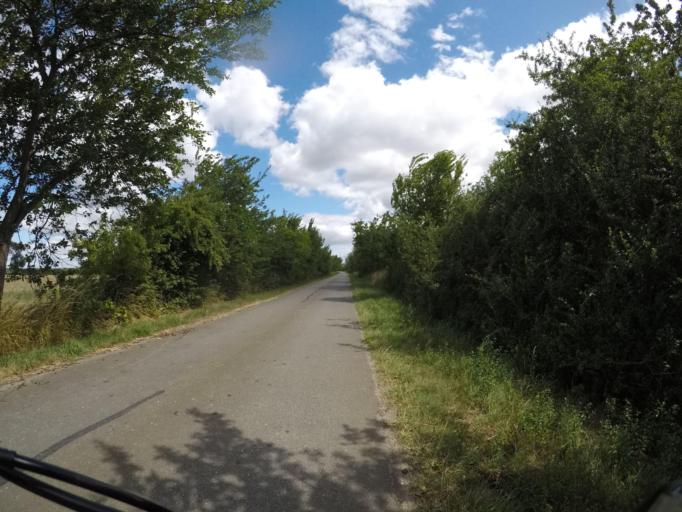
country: DE
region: Lower Saxony
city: Hitzacker
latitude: 53.2100
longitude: 11.0042
